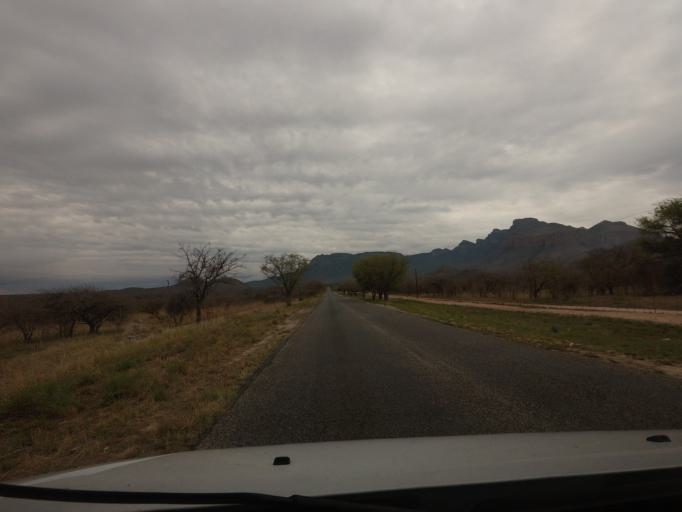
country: ZA
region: Limpopo
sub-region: Mopani District Municipality
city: Hoedspruit
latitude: -24.4840
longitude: 30.8879
